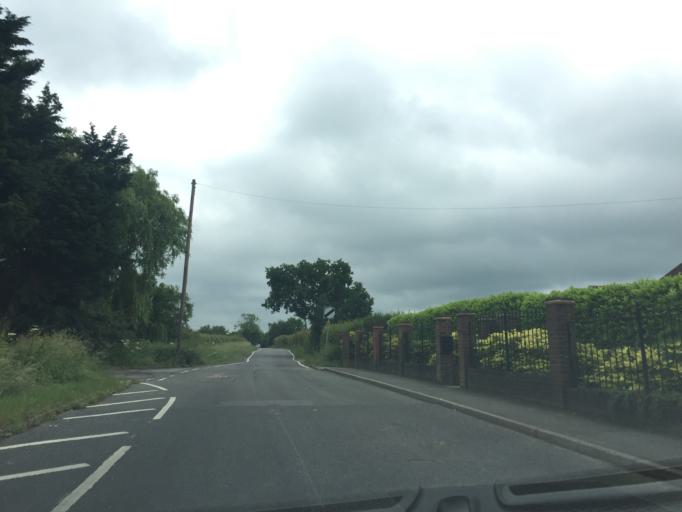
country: GB
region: England
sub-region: Essex
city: Harlow
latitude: 51.7422
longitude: 0.0982
